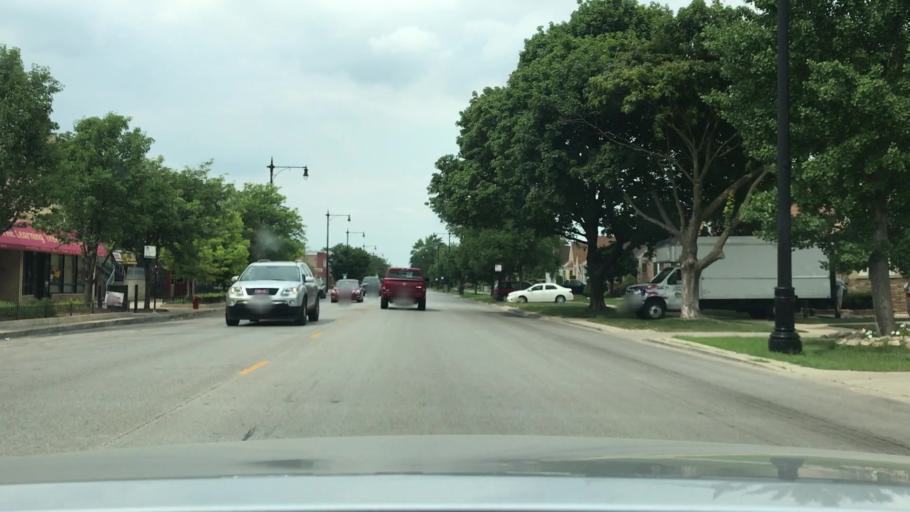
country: US
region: Illinois
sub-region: Cook County
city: Evergreen Park
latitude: 41.7450
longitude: -87.7022
